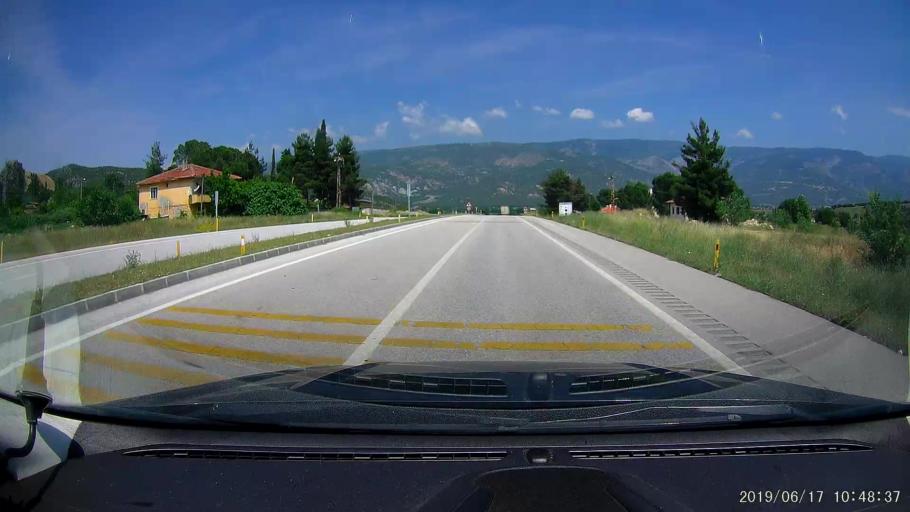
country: TR
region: Corum
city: Hacihamza
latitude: 41.0911
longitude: 34.4258
